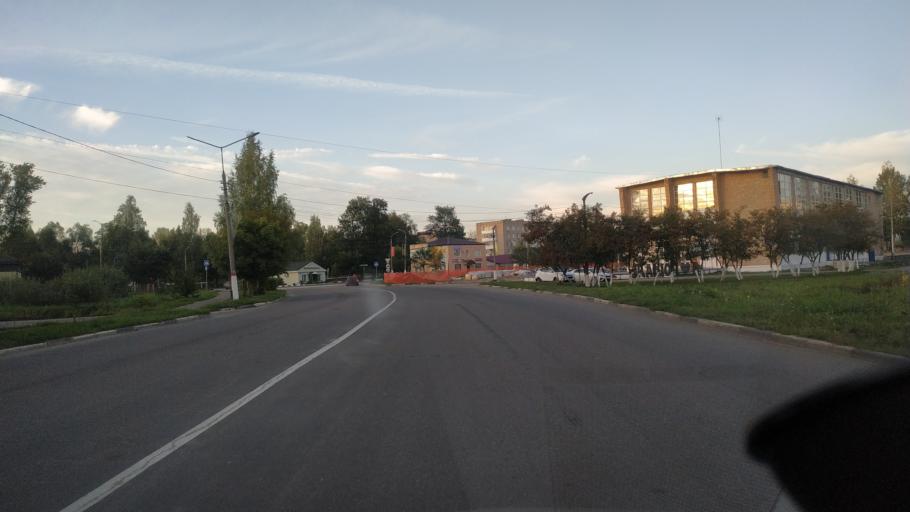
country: RU
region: Moskovskaya
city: Roshal'
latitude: 55.6624
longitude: 39.8581
